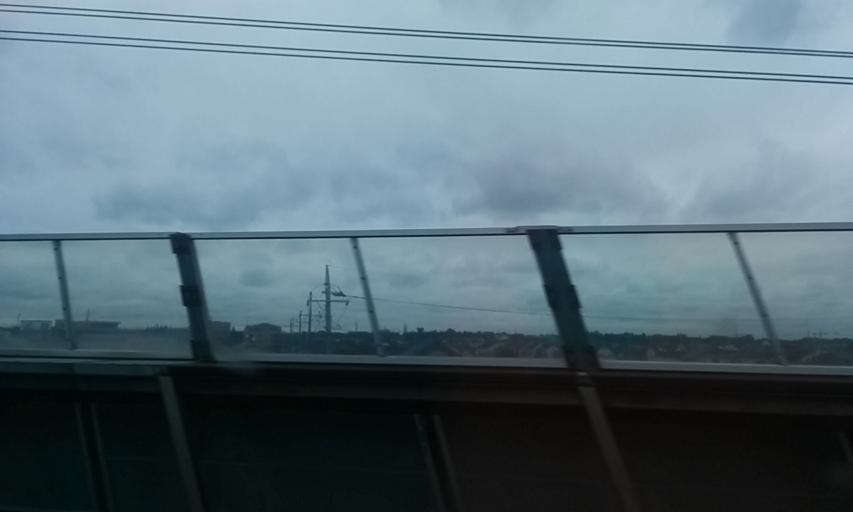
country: JP
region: Ibaraki
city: Koga
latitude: 36.1793
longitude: 139.7390
